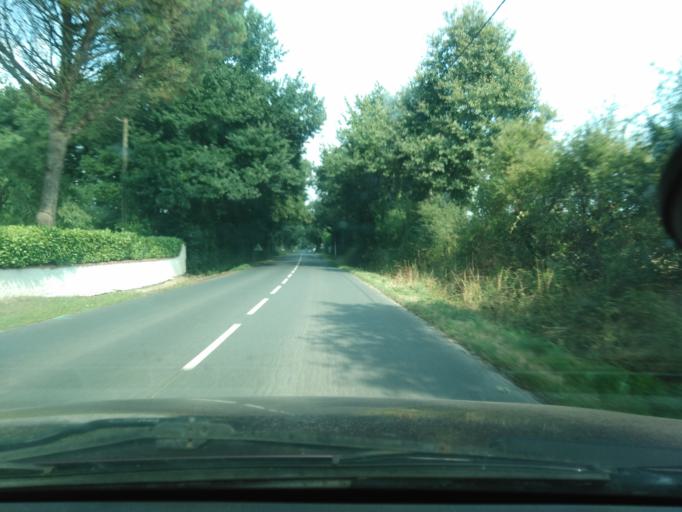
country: FR
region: Pays de la Loire
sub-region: Departement de la Vendee
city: La Roche-sur-Yon
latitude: 46.6416
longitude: -1.4535
